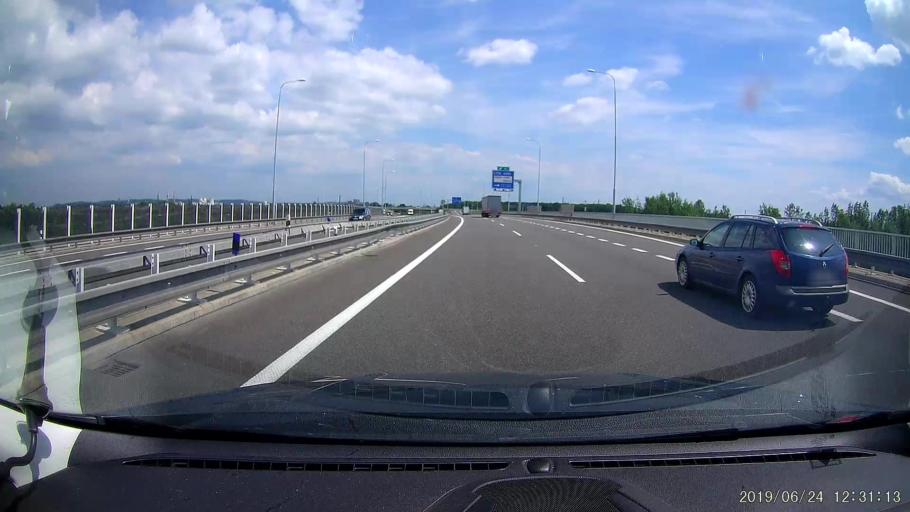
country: CZ
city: Klimkovice
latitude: 49.8052
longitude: 18.2015
